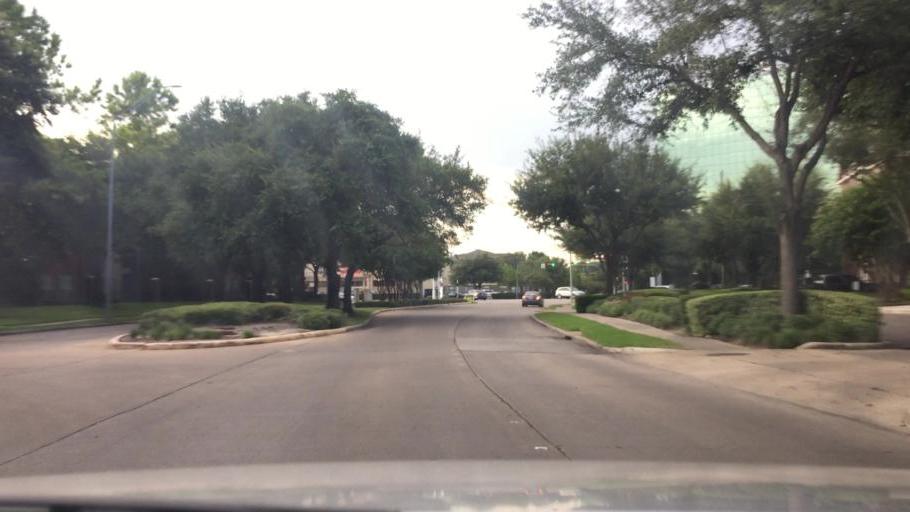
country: US
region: Texas
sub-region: Harris County
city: Bunker Hill Village
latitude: 29.7355
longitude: -95.5809
